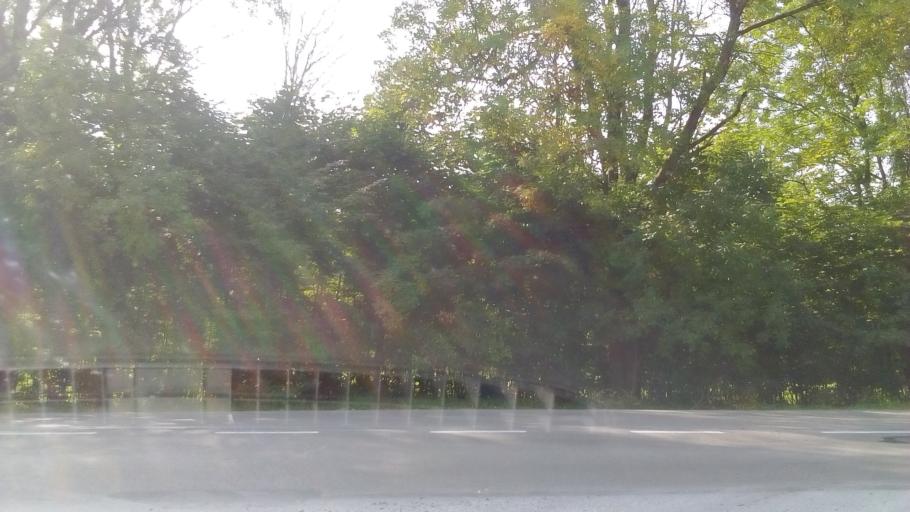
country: LT
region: Alytaus apskritis
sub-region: Alytus
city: Alytus
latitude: 54.3868
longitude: 24.0153
